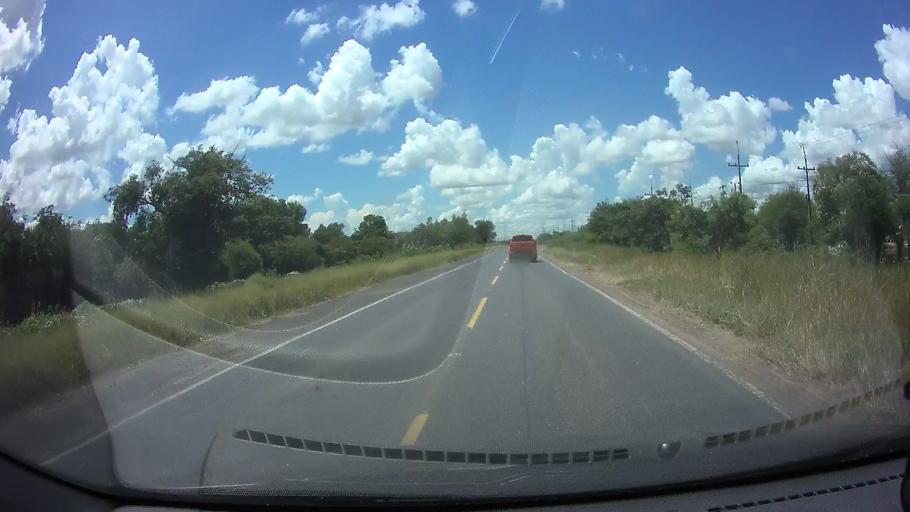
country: PY
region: Central
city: Colonia Mariano Roque Alonso
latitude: -25.1833
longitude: -57.5910
